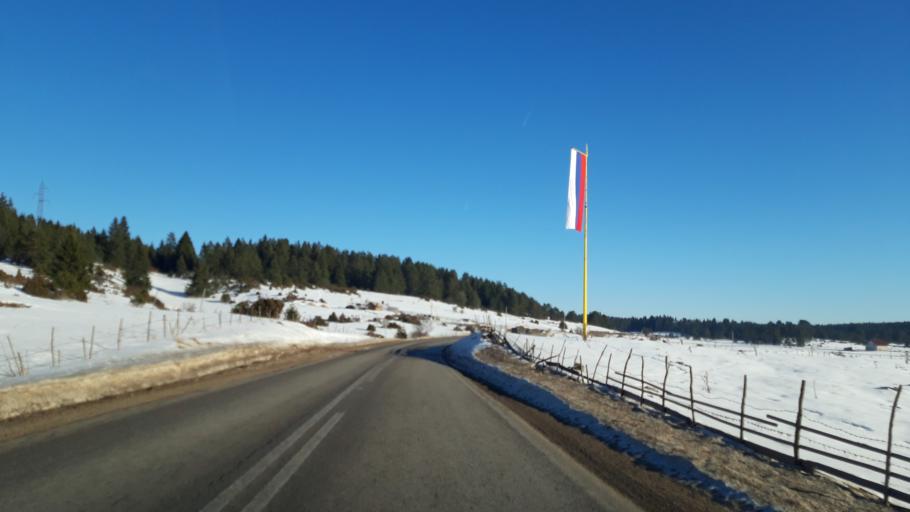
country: BA
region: Republika Srpska
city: Sokolac
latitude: 43.9222
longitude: 18.6802
